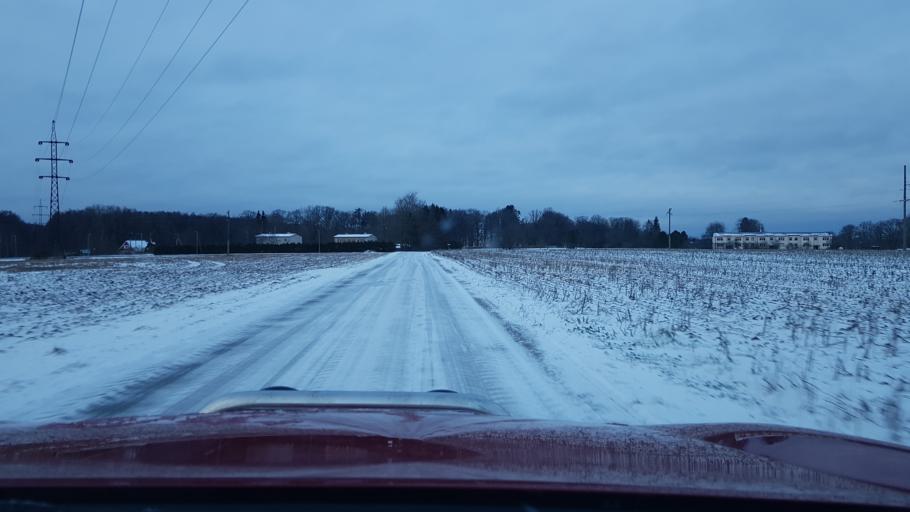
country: EE
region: Harju
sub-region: Maardu linn
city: Maardu
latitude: 59.4238
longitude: 25.0213
